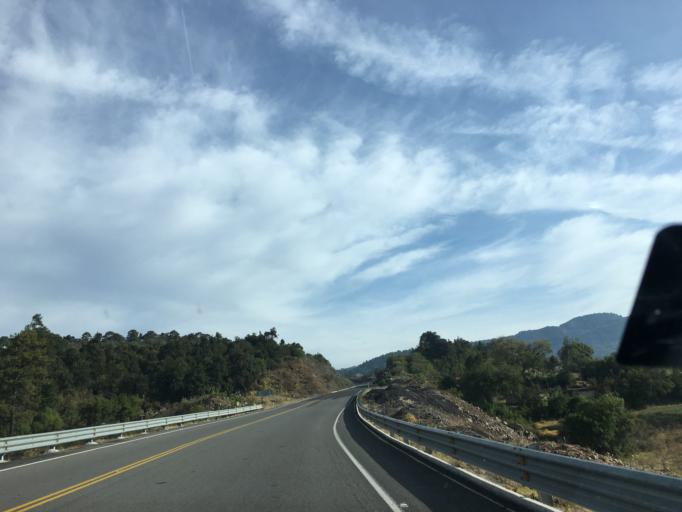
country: MX
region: Mexico
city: San Bartolo
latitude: 19.2557
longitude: -100.0676
